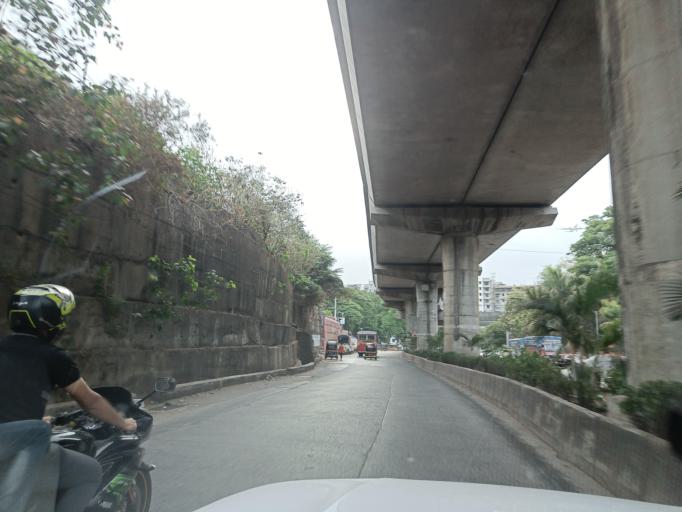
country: IN
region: Maharashtra
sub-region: Mumbai Suburban
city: Powai
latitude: 19.0912
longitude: 72.9057
